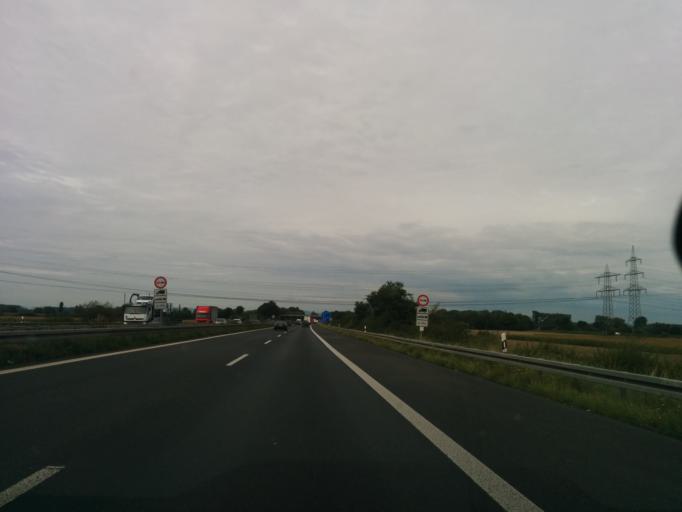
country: DE
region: Baden-Wuerttemberg
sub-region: Karlsruhe Region
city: Neulussheim
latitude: 49.3310
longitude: 8.5170
